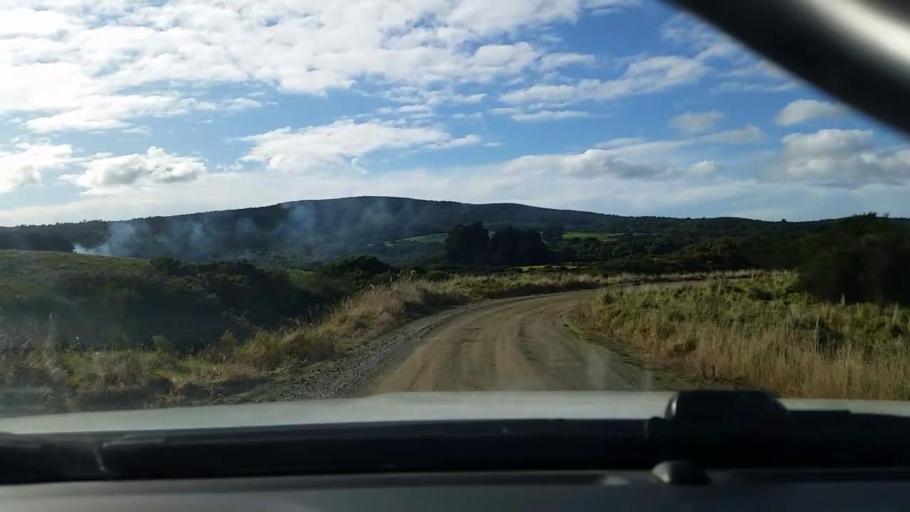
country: NZ
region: Southland
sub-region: Southland District
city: Riverton
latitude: -46.3330
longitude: 167.8185
